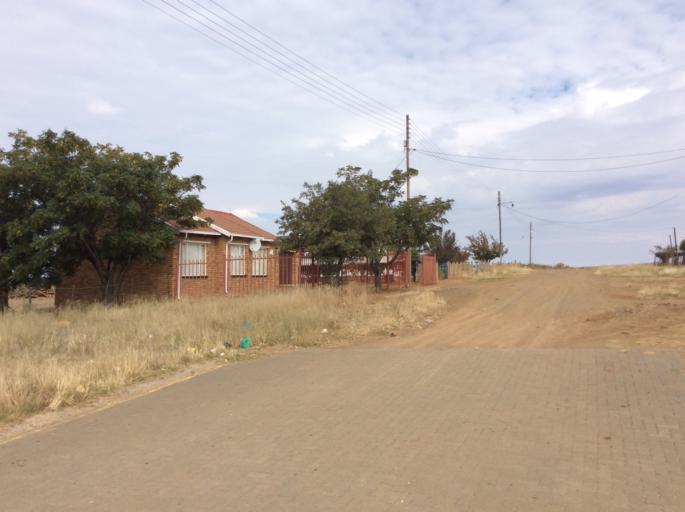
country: LS
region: Mafeteng
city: Mafeteng
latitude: -29.7239
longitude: 27.0110
